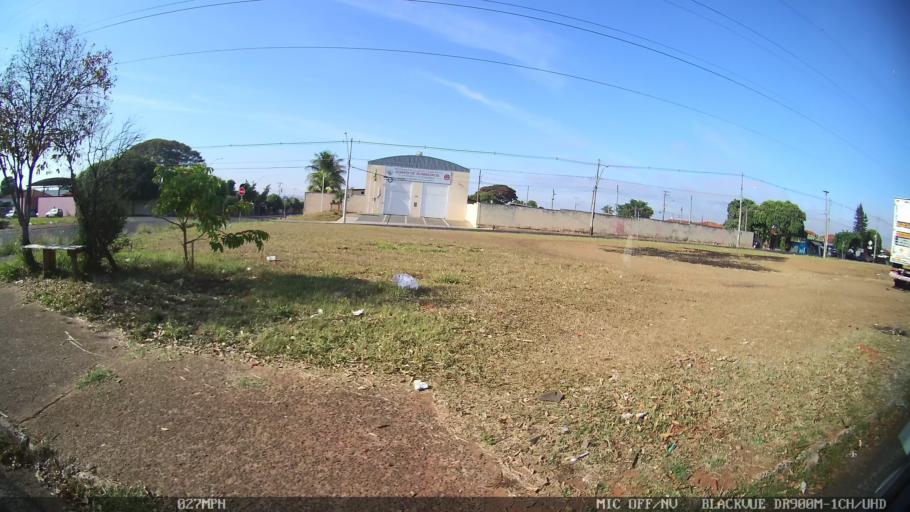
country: BR
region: Sao Paulo
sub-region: Sao Jose Do Rio Preto
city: Sao Jose do Rio Preto
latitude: -20.7803
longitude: -49.4047
